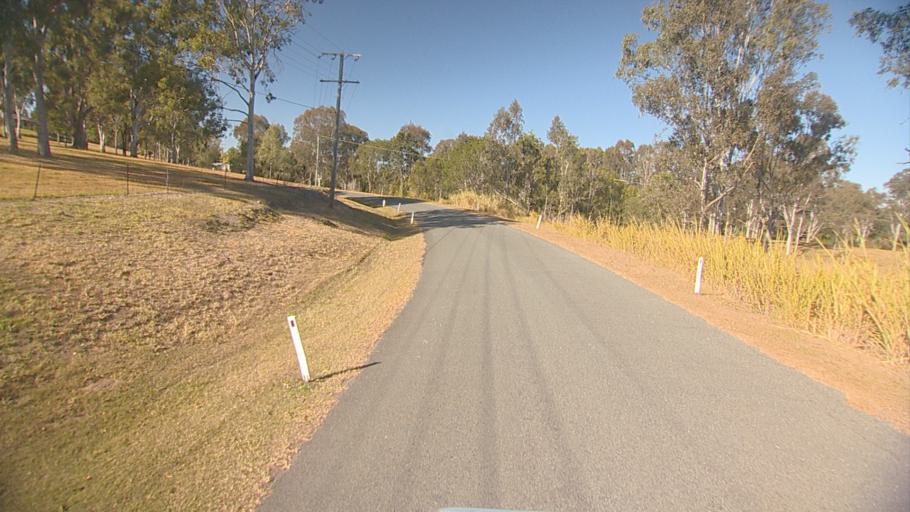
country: AU
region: Queensland
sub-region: Logan
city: North Maclean
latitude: -27.7889
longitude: 153.0064
